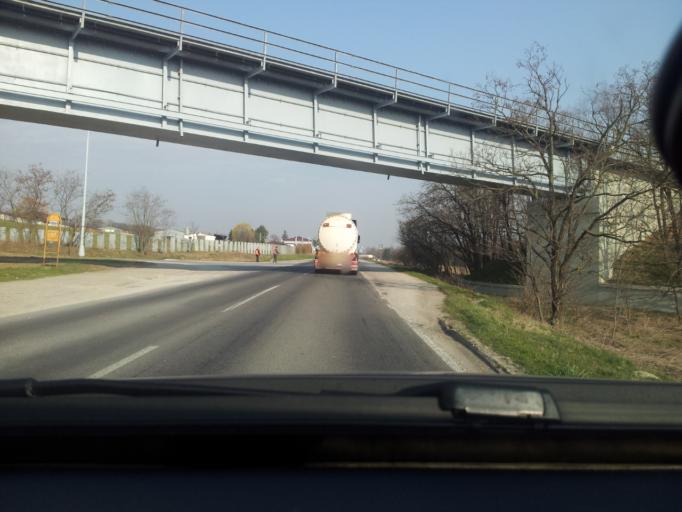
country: SK
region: Trnavsky
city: Hlohovec
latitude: 48.3820
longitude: 17.8713
